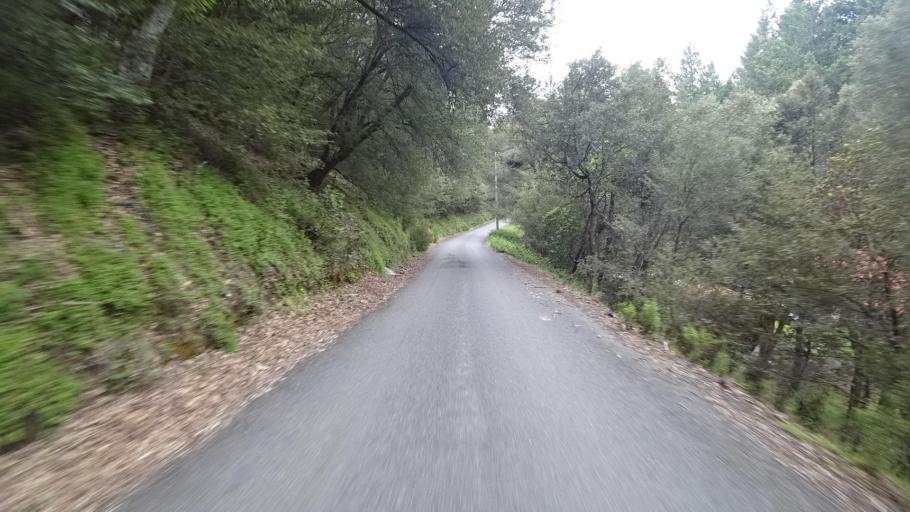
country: US
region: California
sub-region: Humboldt County
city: Willow Creek
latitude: 40.9322
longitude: -123.6152
